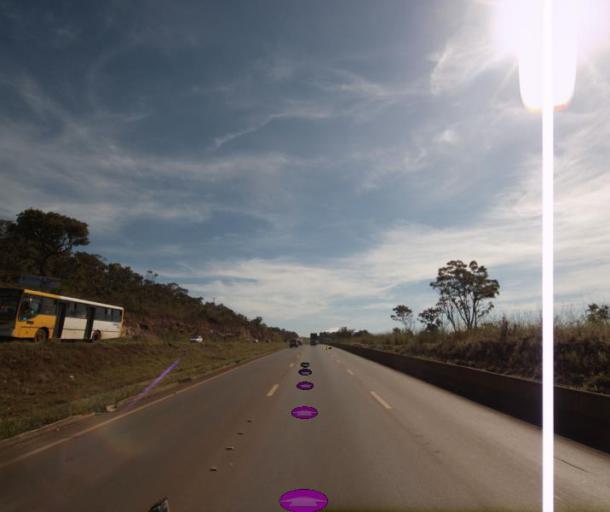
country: BR
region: Federal District
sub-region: Brasilia
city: Brasilia
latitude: -15.7775
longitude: -48.2334
